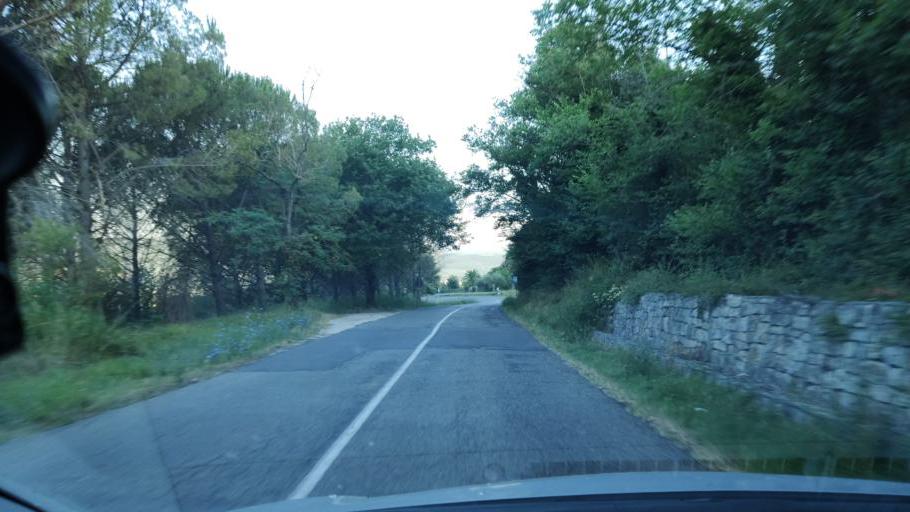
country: IT
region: Umbria
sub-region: Provincia di Terni
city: Giove
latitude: 42.5061
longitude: 12.3214
